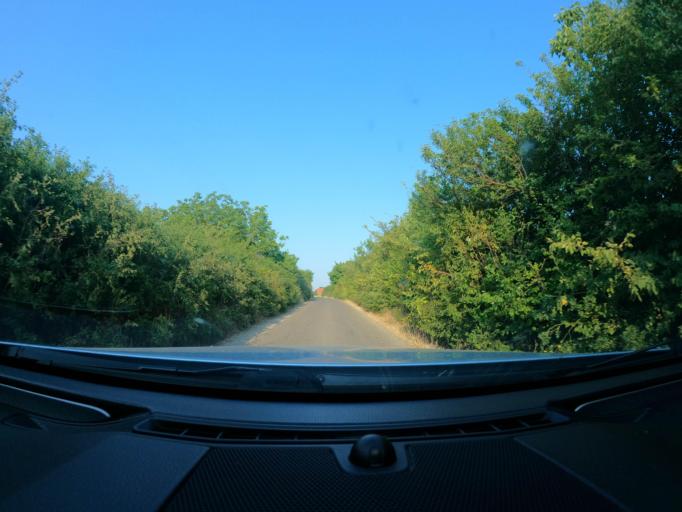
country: RS
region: Autonomna Pokrajina Vojvodina
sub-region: Sremski Okrug
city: Ruma
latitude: 45.0519
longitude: 19.7803
